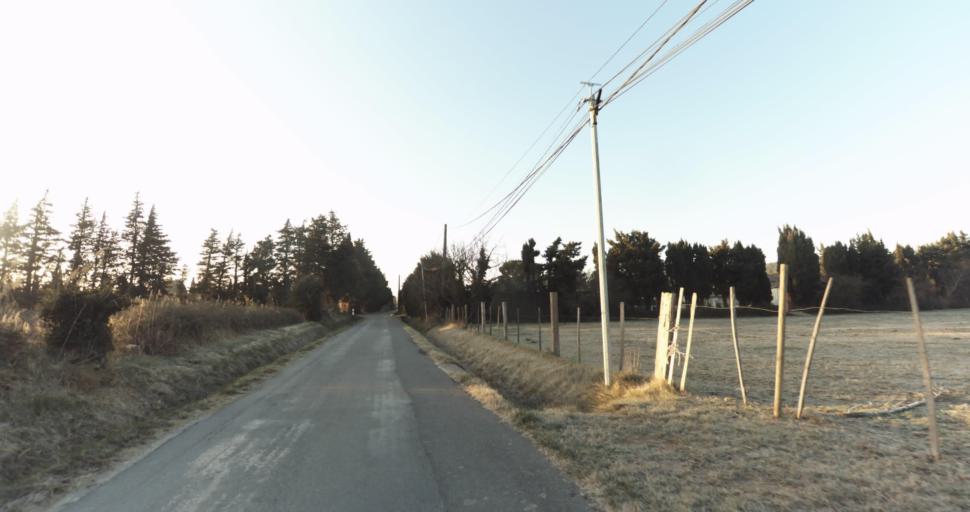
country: FR
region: Provence-Alpes-Cote d'Azur
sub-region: Departement des Bouches-du-Rhone
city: Barbentane
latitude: 43.8861
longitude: 4.7727
